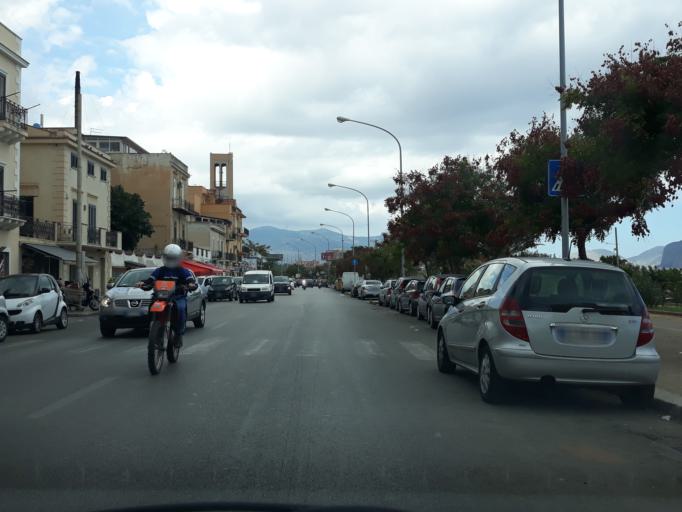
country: IT
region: Sicily
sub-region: Palermo
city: Ciaculli
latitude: 38.1049
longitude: 13.3898
